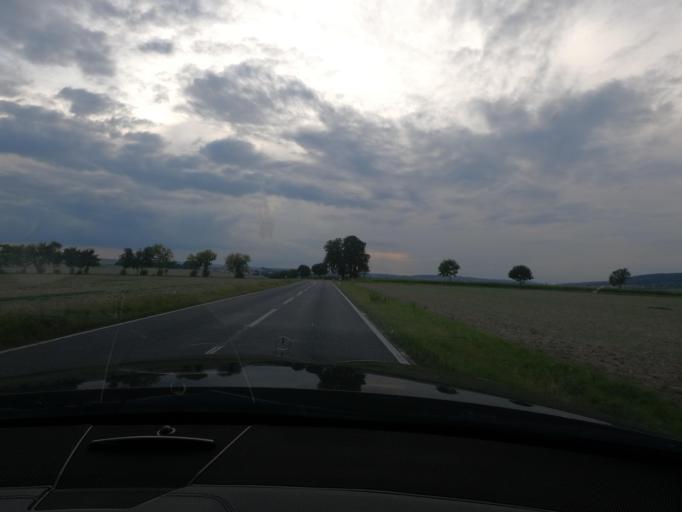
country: DE
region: Thuringia
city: Breitenworbis
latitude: 51.3997
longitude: 10.4255
